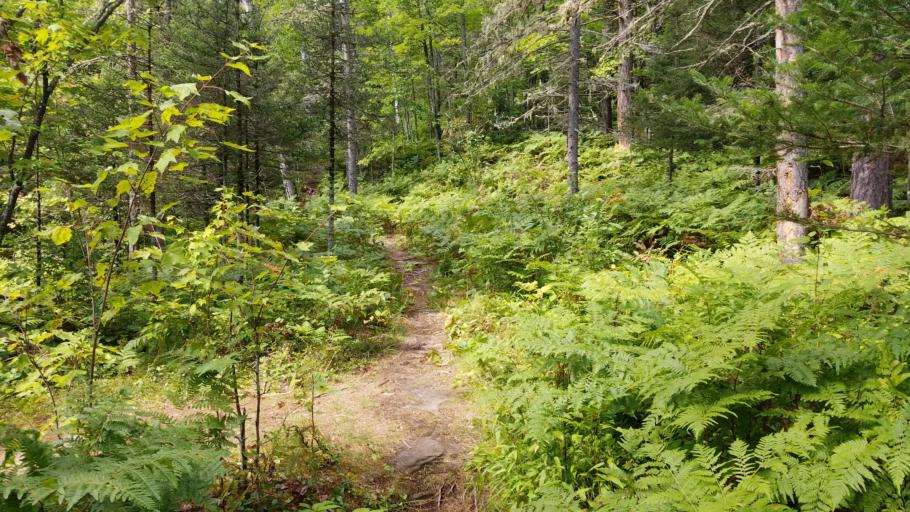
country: US
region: Michigan
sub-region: Ontonagon County
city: Ontonagon
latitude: 46.6517
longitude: -89.1515
